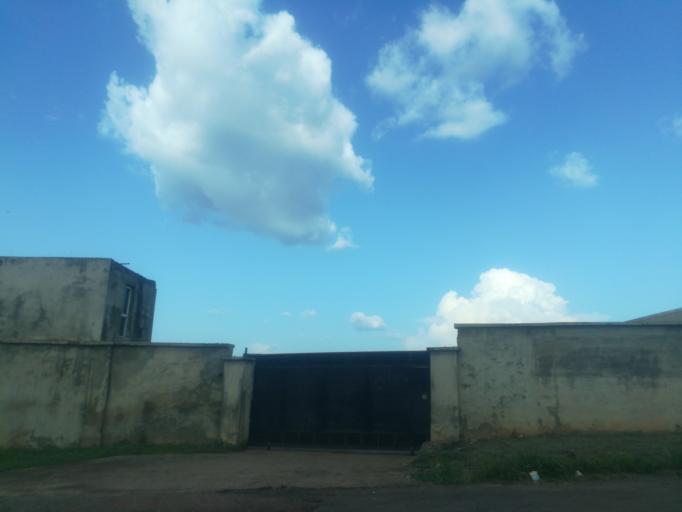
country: NG
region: Oyo
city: Ibadan
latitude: 7.4015
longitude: 3.9626
